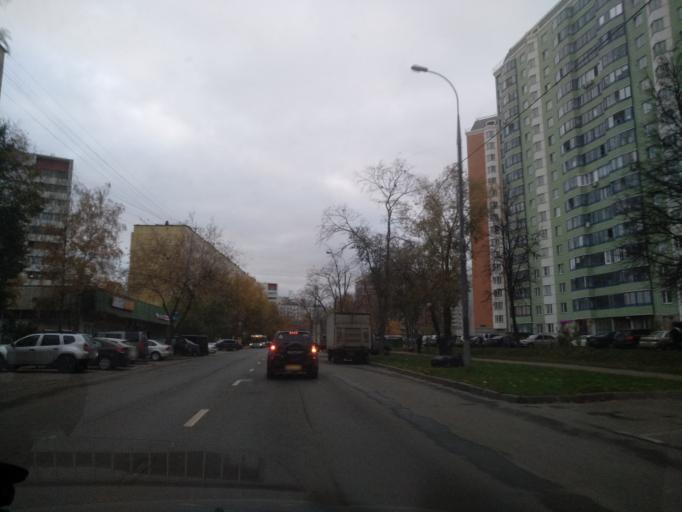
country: RU
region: Moscow
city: Kozeyevo
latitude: 55.8738
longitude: 37.6263
